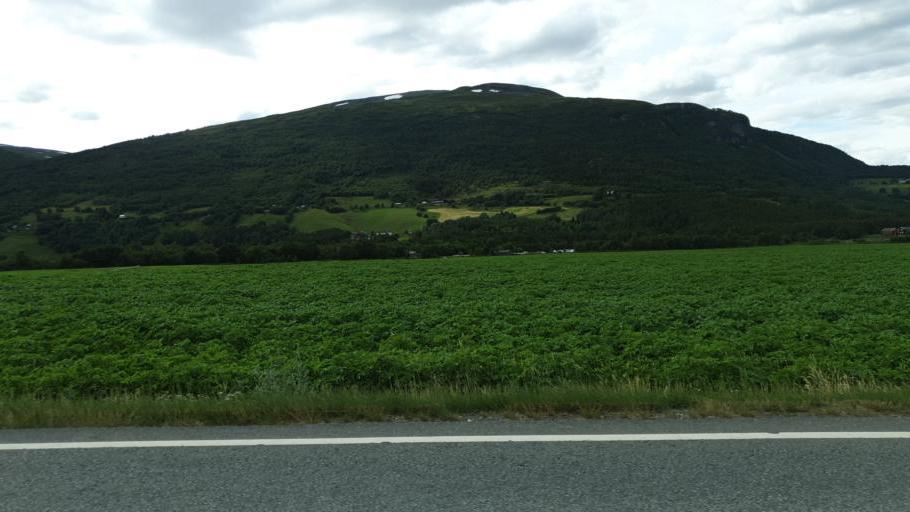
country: NO
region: Sor-Trondelag
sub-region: Oppdal
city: Oppdal
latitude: 62.5372
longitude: 9.6260
